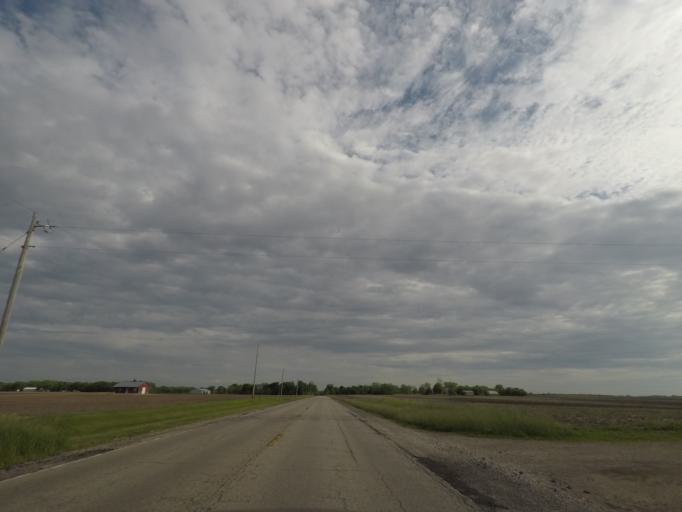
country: US
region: Illinois
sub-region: Logan County
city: Mount Pulaski
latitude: 40.0405
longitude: -89.2816
